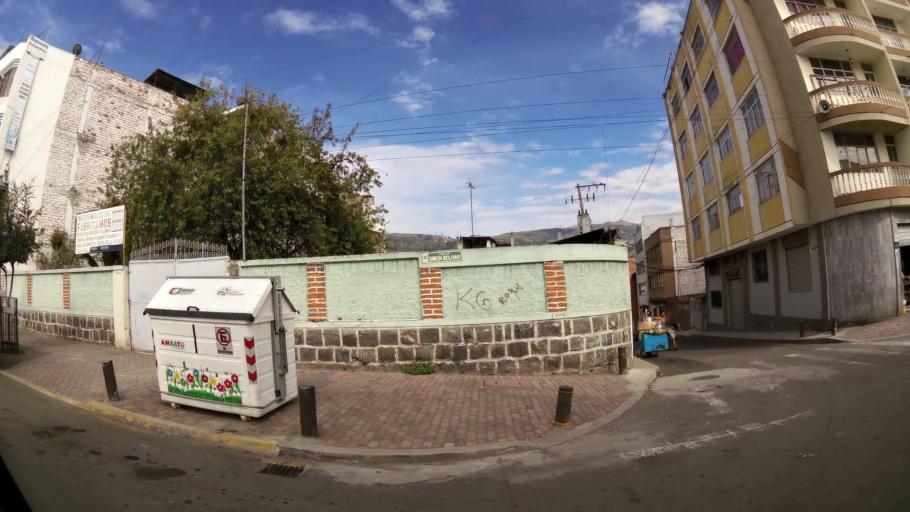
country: EC
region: Tungurahua
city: Ambato
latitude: -1.2397
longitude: -78.6347
